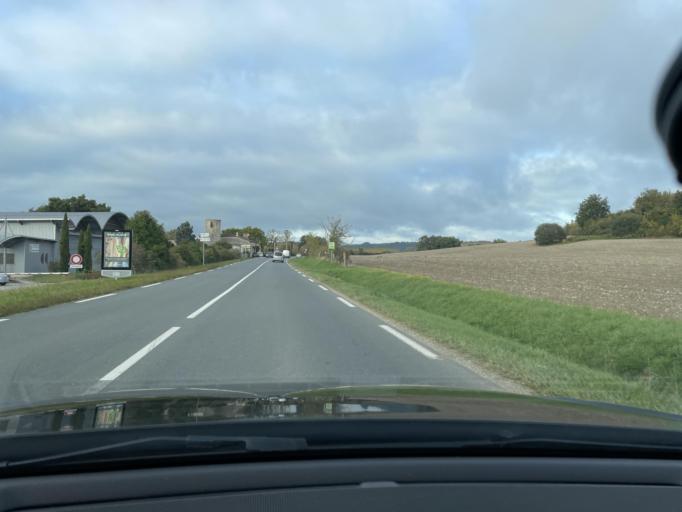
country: FR
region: Aquitaine
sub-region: Departement du Lot-et-Garonne
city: Casteljaloux
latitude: 44.3248
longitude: 0.0959
